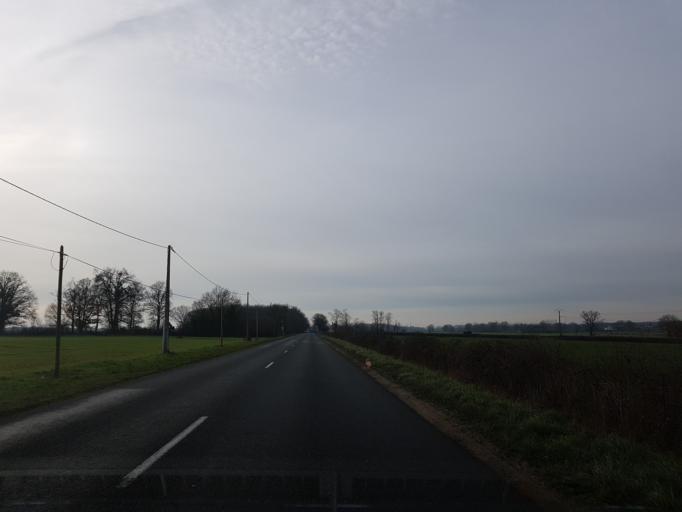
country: FR
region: Auvergne
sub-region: Departement de l'Allier
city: Lusigny
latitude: 46.5825
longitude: 3.4487
